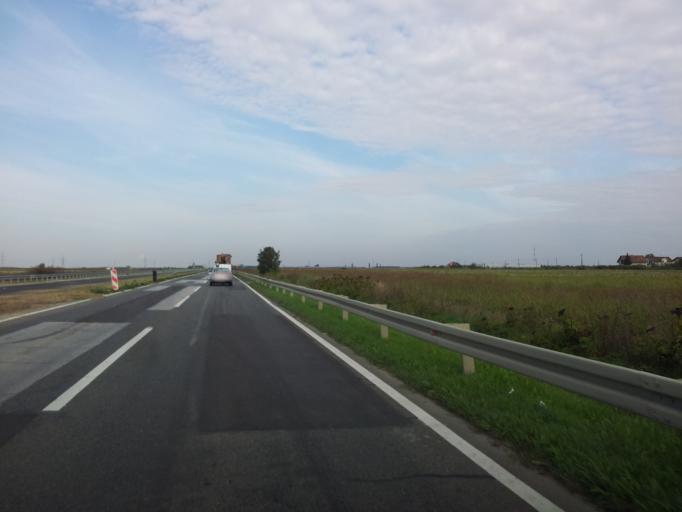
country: HR
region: Osjecko-Baranjska
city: Josipovac
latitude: 45.5683
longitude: 18.5842
